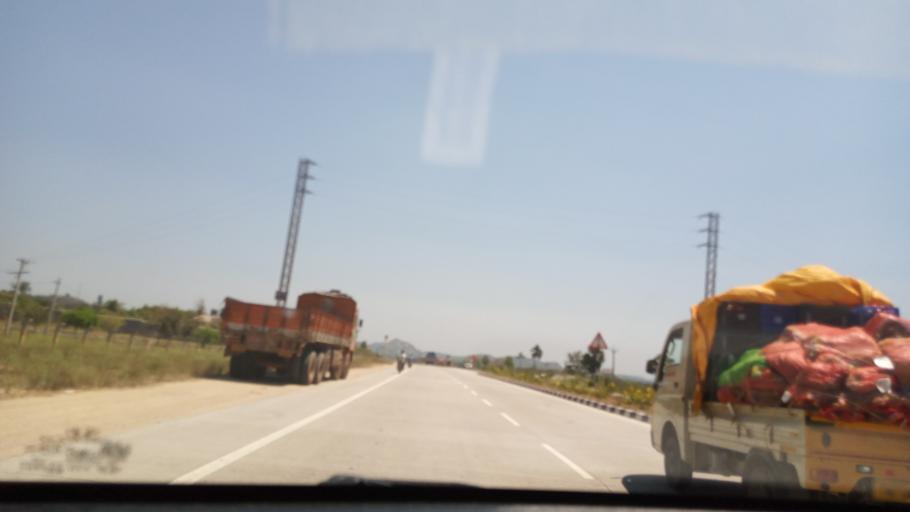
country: IN
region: Andhra Pradesh
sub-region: Chittoor
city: Chittoor
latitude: 13.1940
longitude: 79.0285
